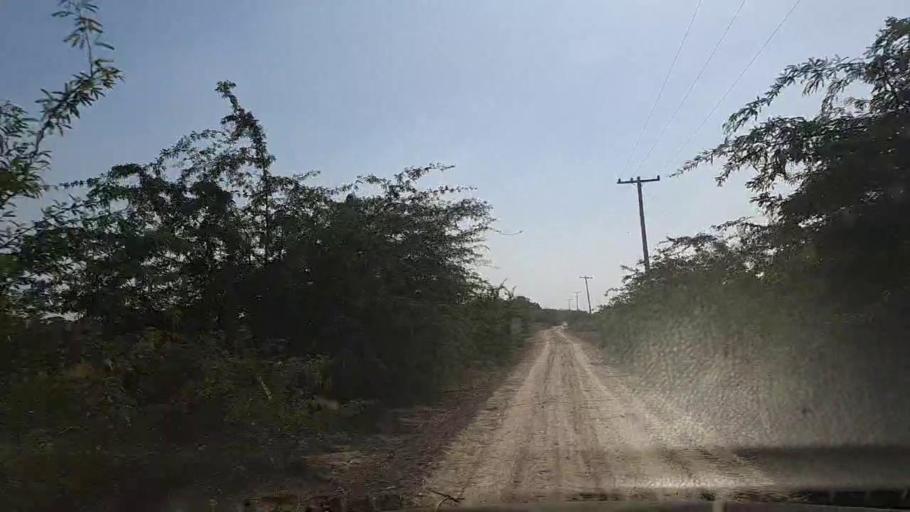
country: PK
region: Sindh
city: Daro Mehar
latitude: 24.7754
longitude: 68.0678
